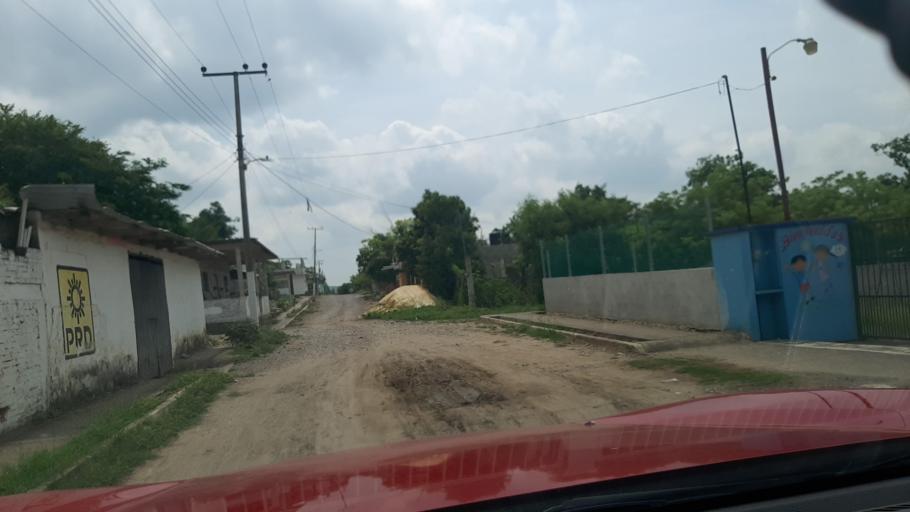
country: MX
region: Veracruz
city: Gutierrez Zamora
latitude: 20.4466
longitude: -97.1640
